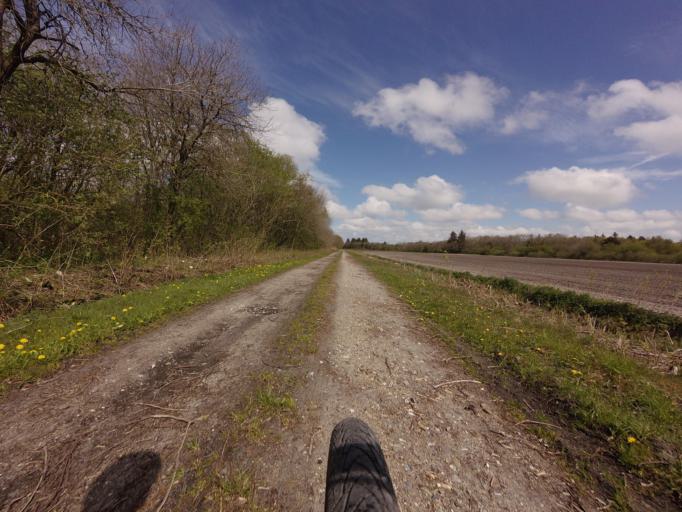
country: DK
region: North Denmark
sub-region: Jammerbugt Kommune
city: Kas
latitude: 57.1891
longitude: 9.5936
